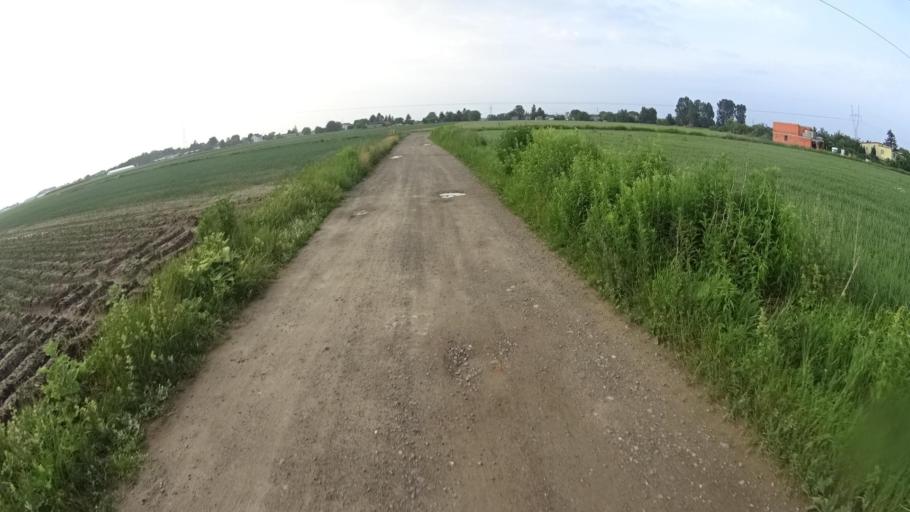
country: PL
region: Masovian Voivodeship
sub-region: Powiat warszawski zachodni
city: Babice
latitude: 52.2211
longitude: 20.8550
